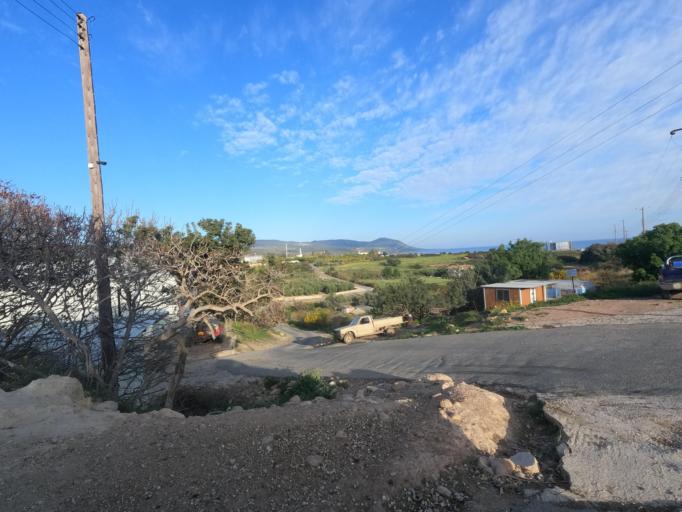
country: CY
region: Pafos
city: Polis
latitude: 35.0328
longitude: 32.3984
